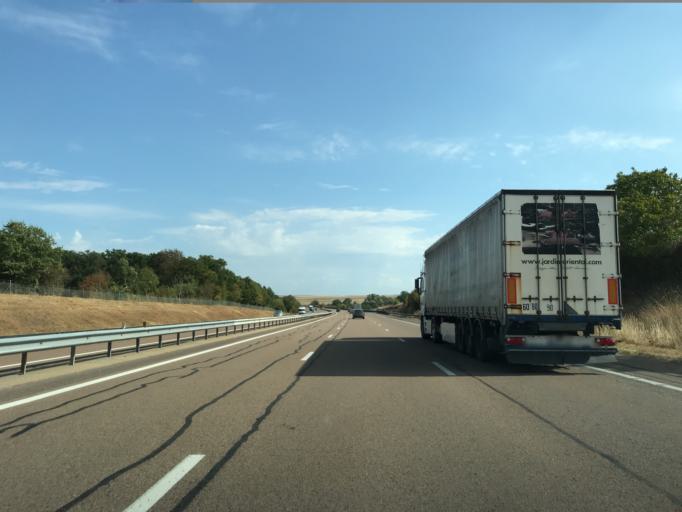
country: FR
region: Bourgogne
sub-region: Departement de l'Yonne
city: Aillant-sur-Tholon
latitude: 47.9043
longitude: 3.3457
